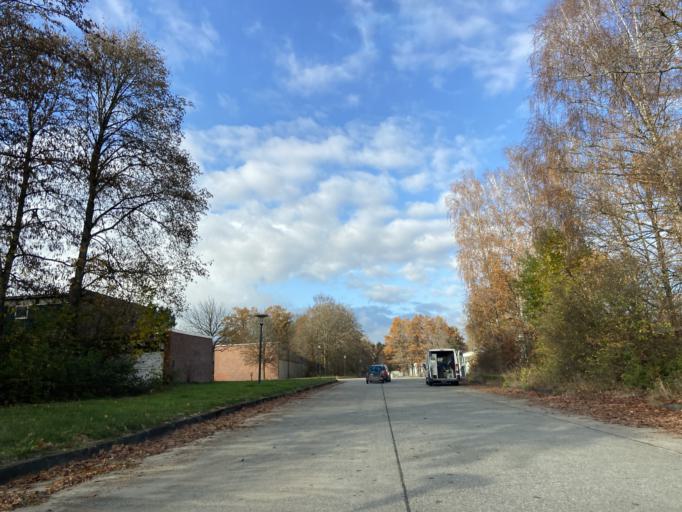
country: DE
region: Baden-Wuerttemberg
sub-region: Tuebingen Region
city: Sigmaringen
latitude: 48.0925
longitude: 9.2502
